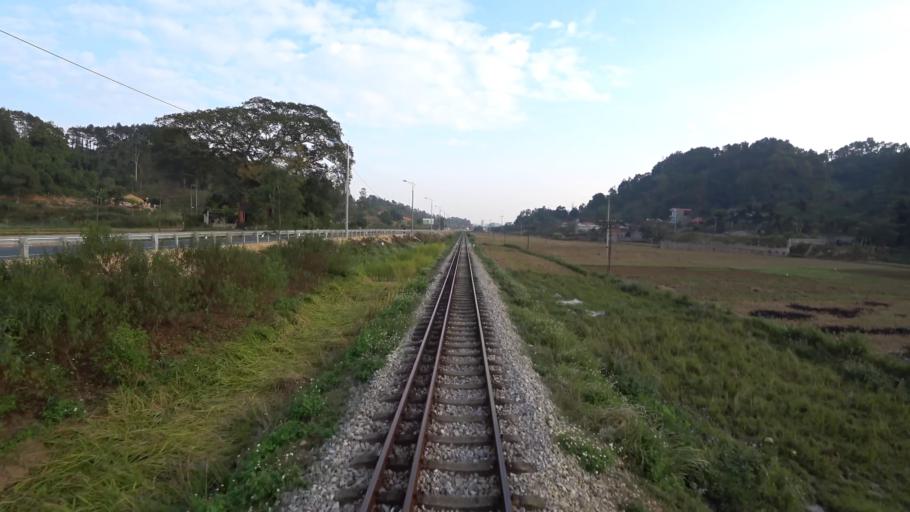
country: VN
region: Lang Son
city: Thi Tran Cao Loc
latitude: 21.9026
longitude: 106.7380
